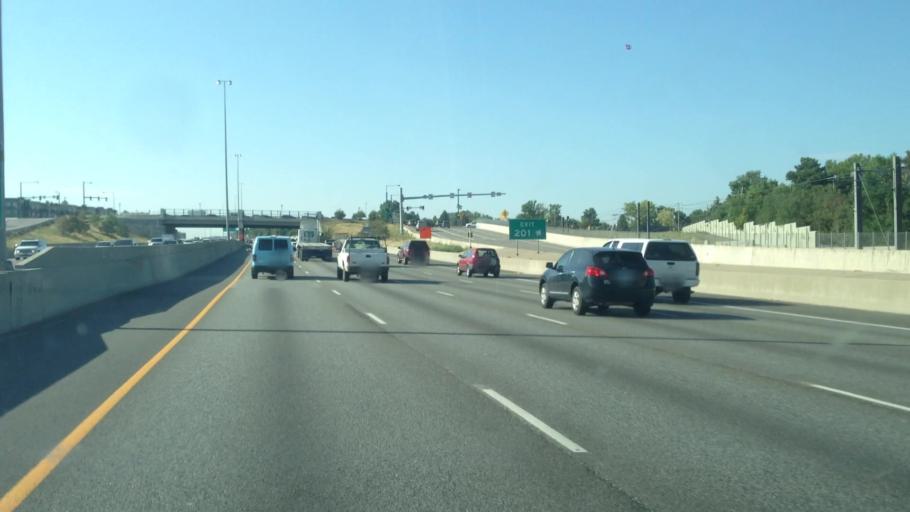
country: US
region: Colorado
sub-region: Arapahoe County
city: Cherry Hills Village
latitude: 39.6557
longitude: -104.9202
